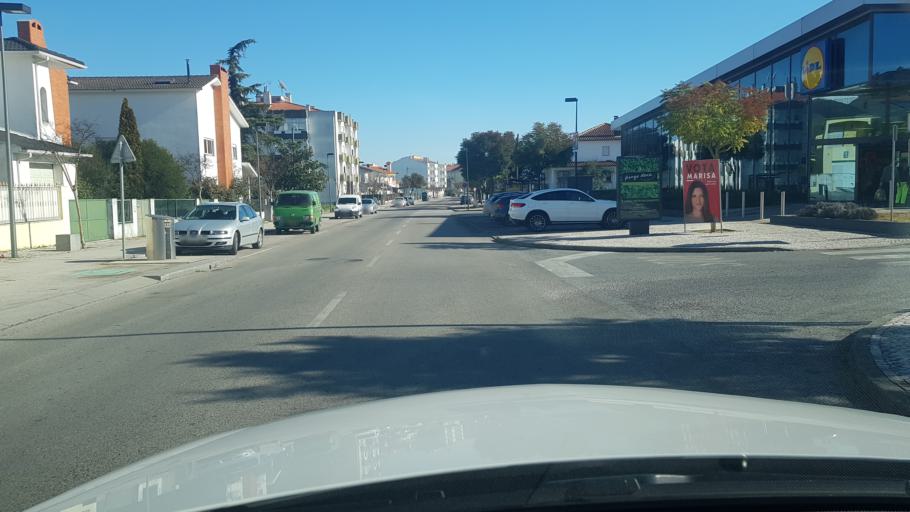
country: PT
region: Santarem
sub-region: Entroncamento
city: Entroncamento
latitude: 39.4733
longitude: -8.4772
